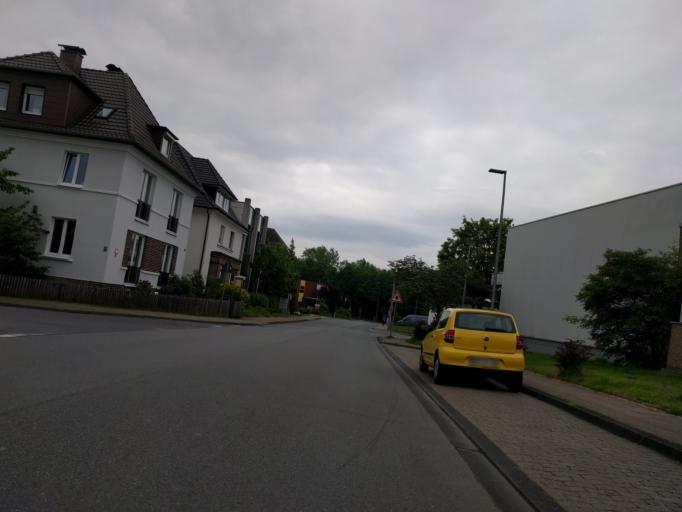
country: DE
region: North Rhine-Westphalia
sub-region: Regierungsbezirk Detmold
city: Bielefeld
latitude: 52.0402
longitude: 8.5779
